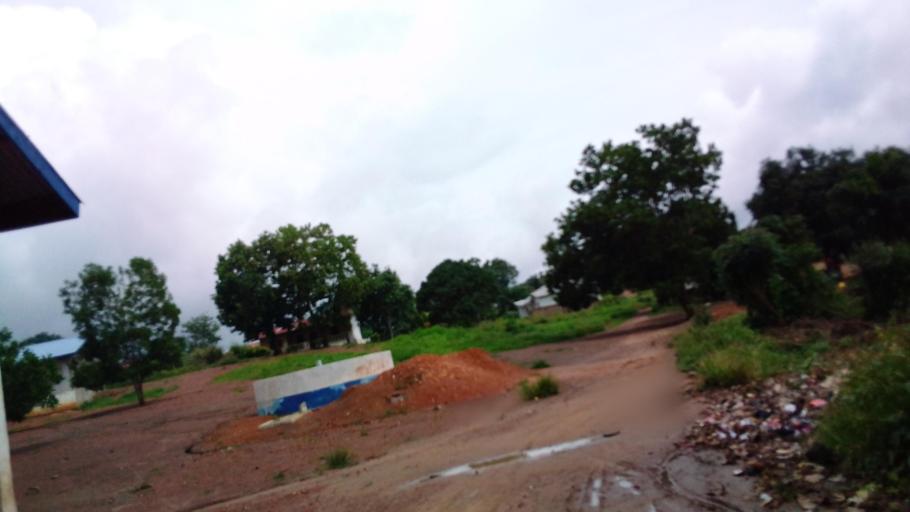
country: SL
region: Eastern Province
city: Kenema
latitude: 7.8625
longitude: -11.1729
